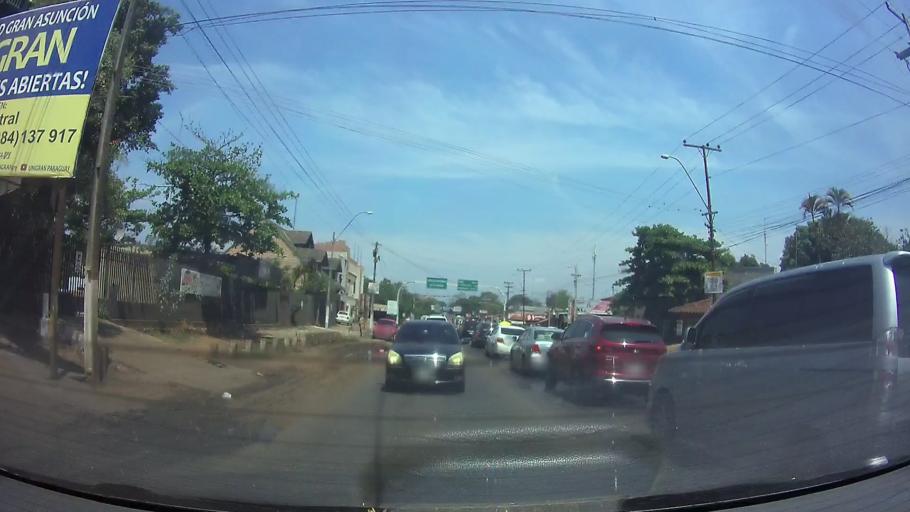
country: PY
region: Central
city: Capiata
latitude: -25.4177
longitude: -57.4560
